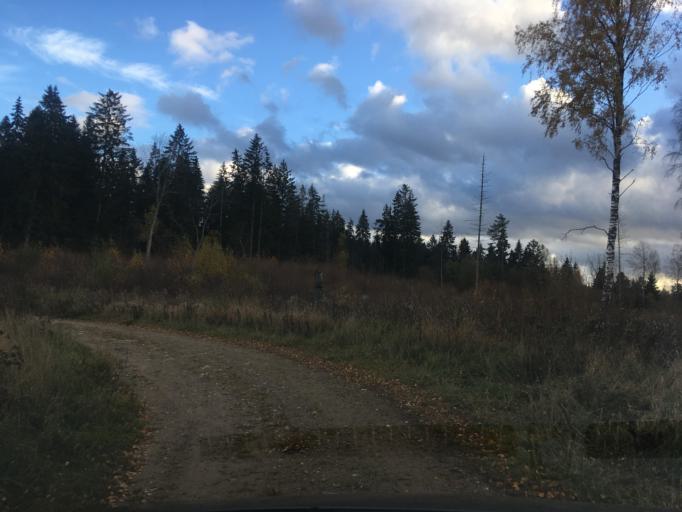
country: EE
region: Harju
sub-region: Raasiku vald
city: Arukula
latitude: 59.3580
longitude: 25.1025
